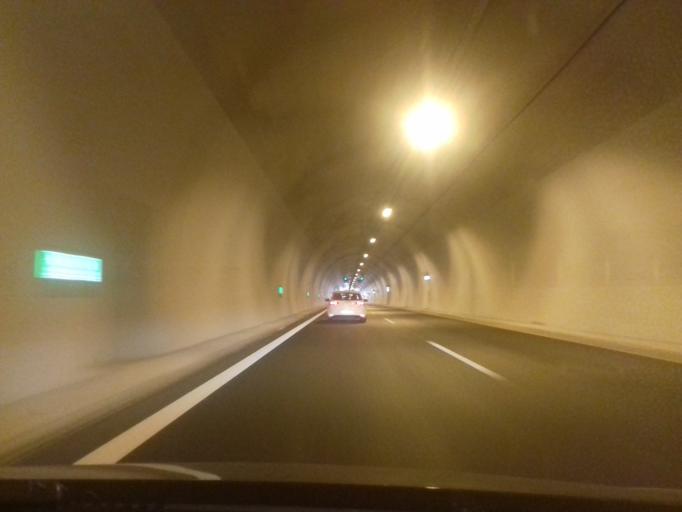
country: GR
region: West Greece
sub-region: Nomos Achaias
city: Aiyira
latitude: 38.1370
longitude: 22.3834
